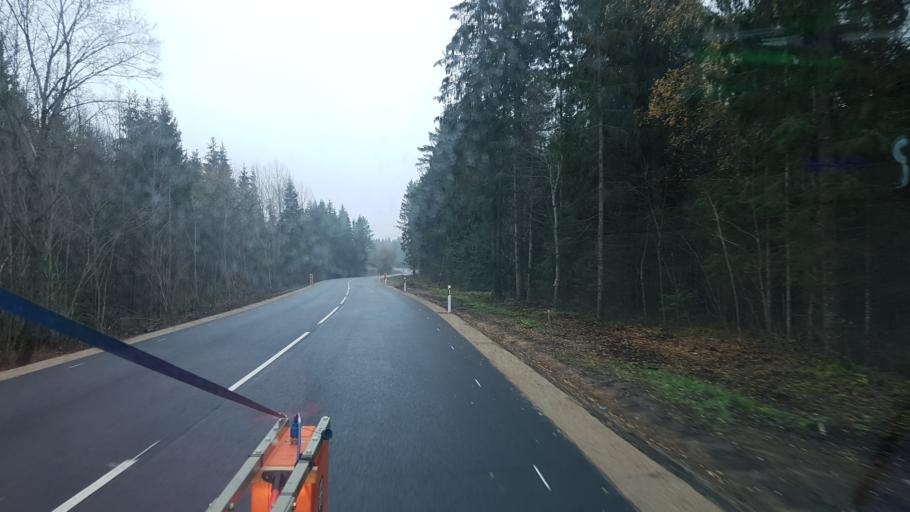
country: EE
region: Raplamaa
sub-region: Kohila vald
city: Kohila
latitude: 59.1783
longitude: 24.7886
